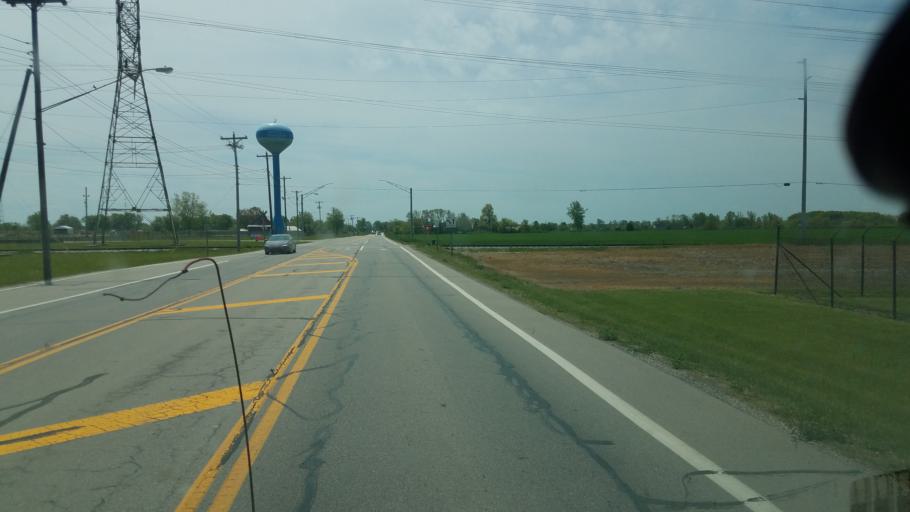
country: US
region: Ohio
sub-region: Ottawa County
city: Oak Harbor
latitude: 41.5955
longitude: -83.0968
